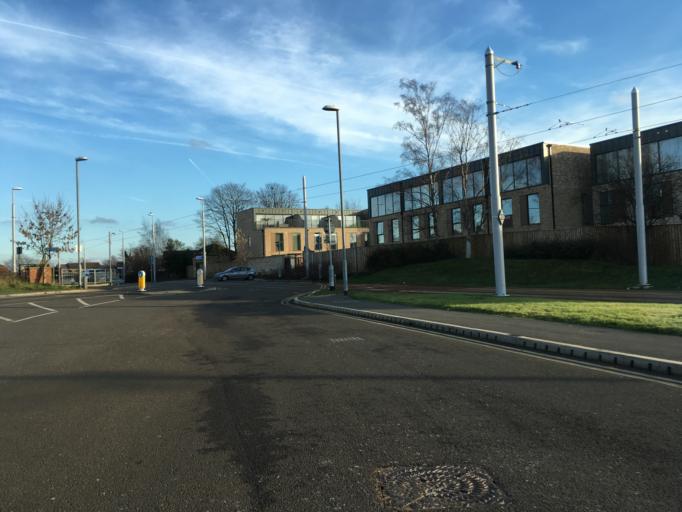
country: GB
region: England
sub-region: Manchester
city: Chorlton cum Hardy
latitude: 53.4304
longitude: -2.2791
